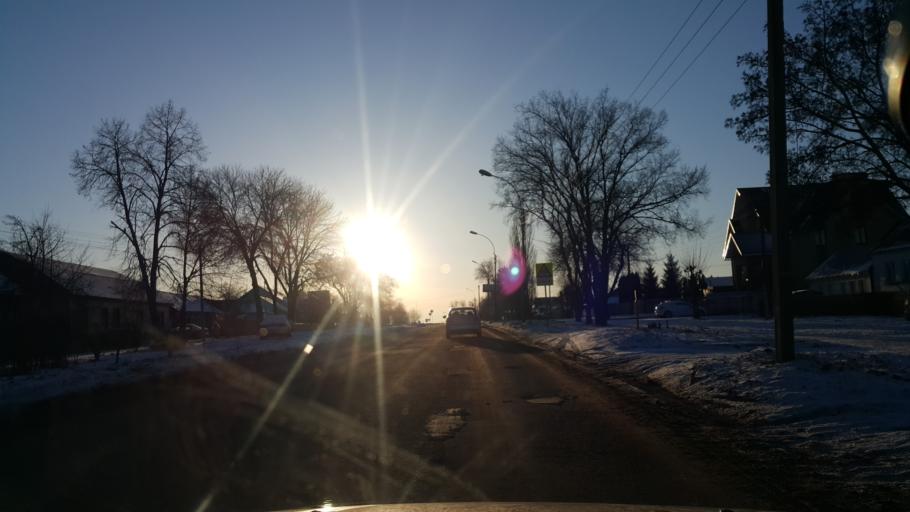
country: RU
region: Tambov
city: Pokrovo-Prigorodnoye
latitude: 52.7078
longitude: 41.4153
